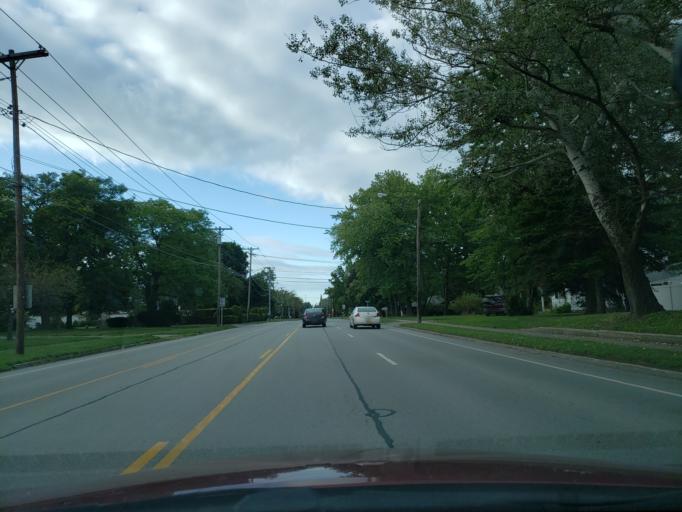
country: US
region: New York
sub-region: Monroe County
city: Greece
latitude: 43.2425
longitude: -77.6591
